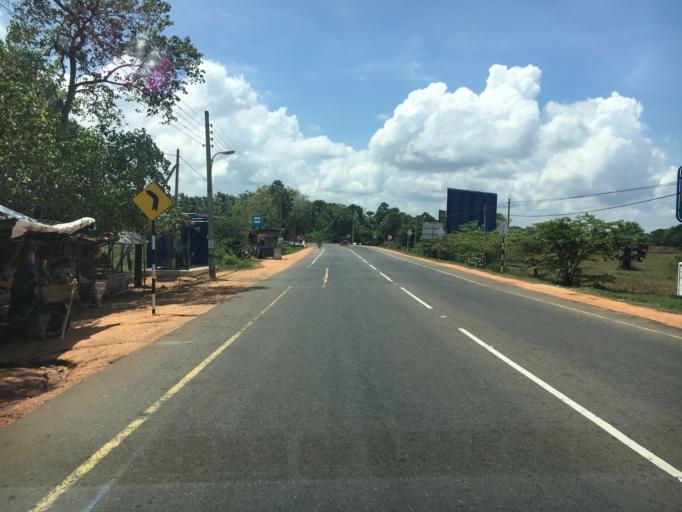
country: LK
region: North Central
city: Anuradhapura
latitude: 8.2737
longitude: 80.5003
